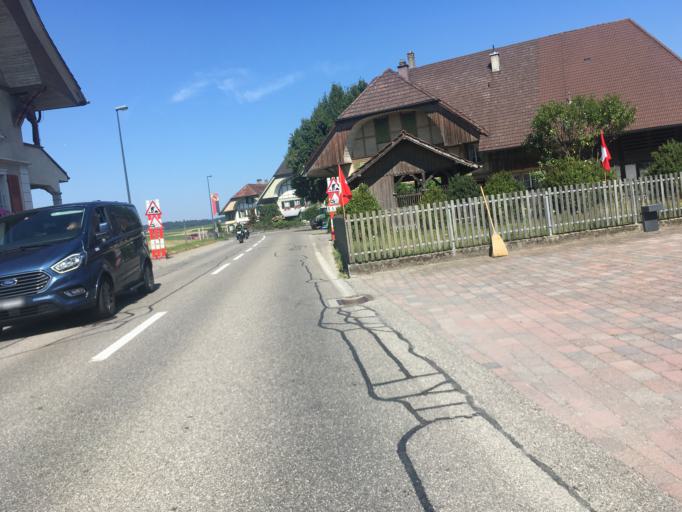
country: CH
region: Bern
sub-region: Bern-Mittelland District
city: Fraubrunnen
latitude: 47.0744
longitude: 7.5386
